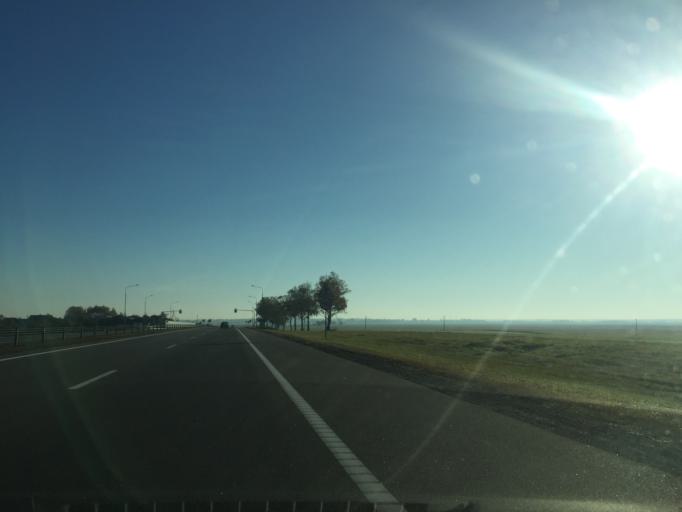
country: BY
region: Minsk
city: Smilavichy
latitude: 53.7616
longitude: 27.9287
